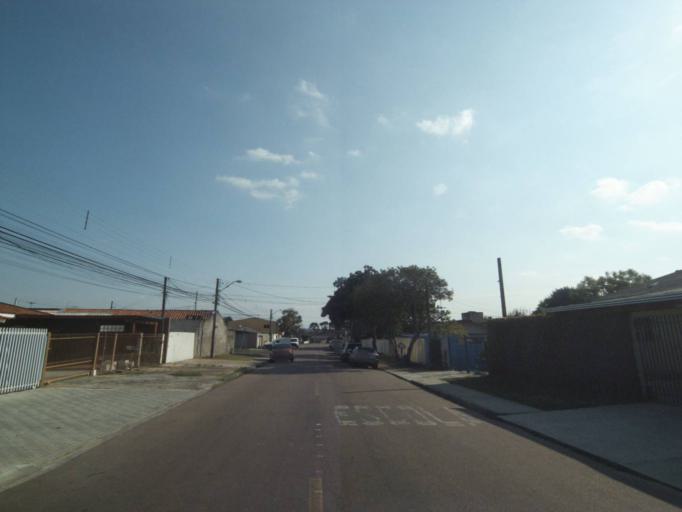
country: BR
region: Parana
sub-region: Curitiba
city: Curitiba
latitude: -25.4894
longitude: -49.3313
